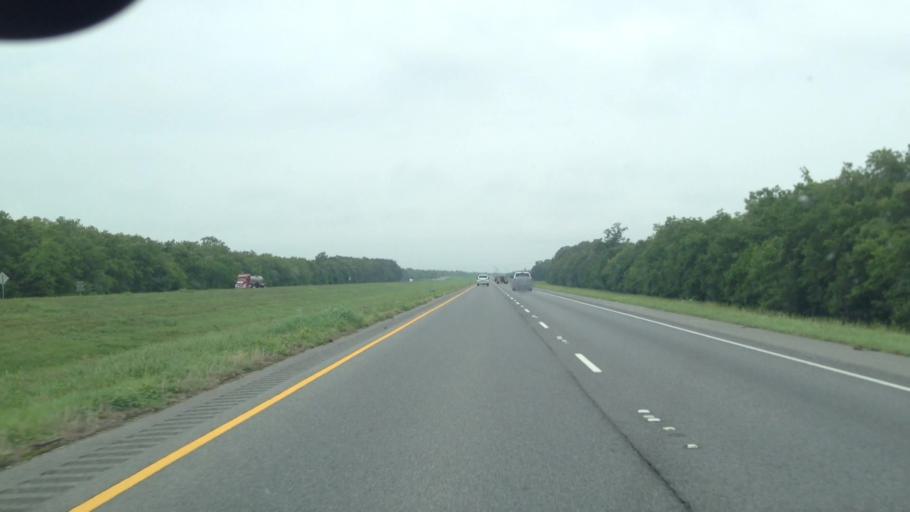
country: US
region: Louisiana
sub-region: Evangeline Parish
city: Ville Platte
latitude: 30.7182
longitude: -92.1084
